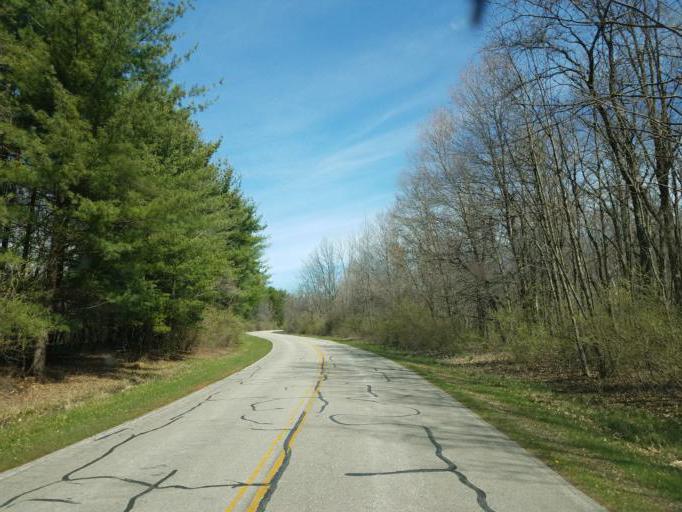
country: US
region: Ohio
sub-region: Delaware County
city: Delaware
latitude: 40.3849
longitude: -83.0667
